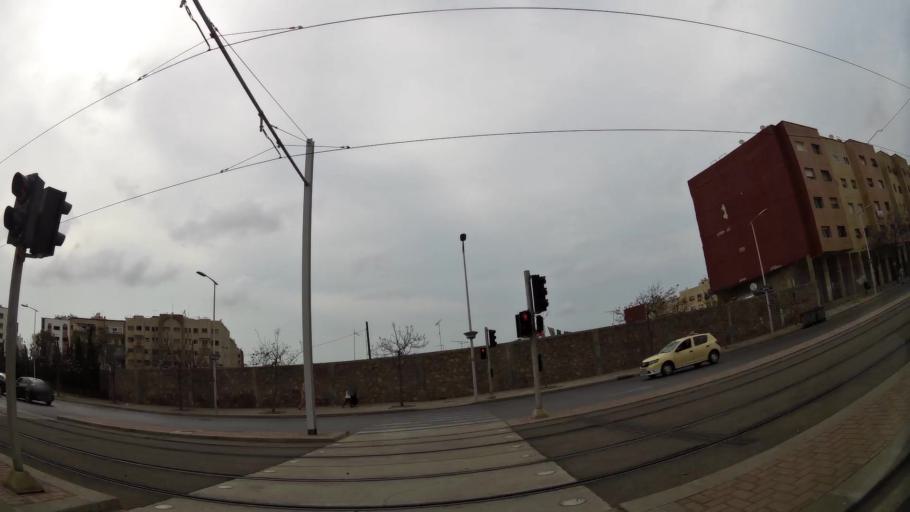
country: MA
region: Rabat-Sale-Zemmour-Zaer
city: Sale
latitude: 34.0468
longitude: -6.8020
